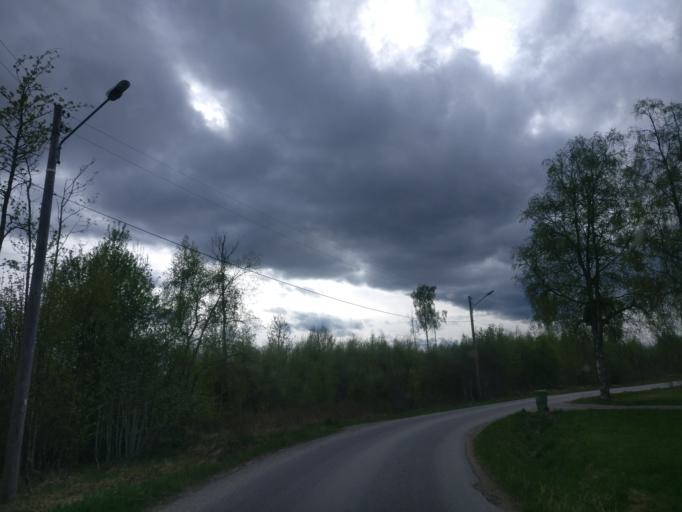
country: SE
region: Vaesternorrland
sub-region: Timra Kommun
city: Soraker
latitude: 62.5099
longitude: 17.5240
